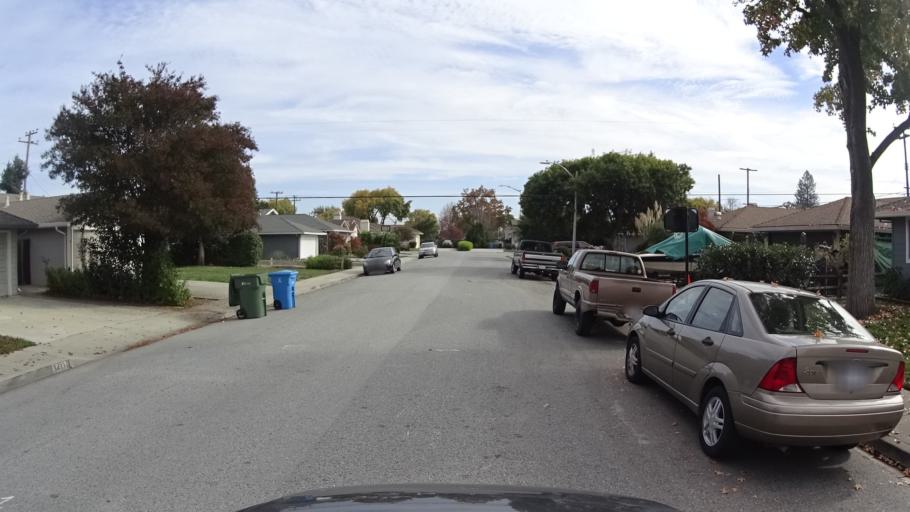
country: US
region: California
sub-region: Santa Clara County
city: Santa Clara
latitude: 37.3277
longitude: -121.9590
